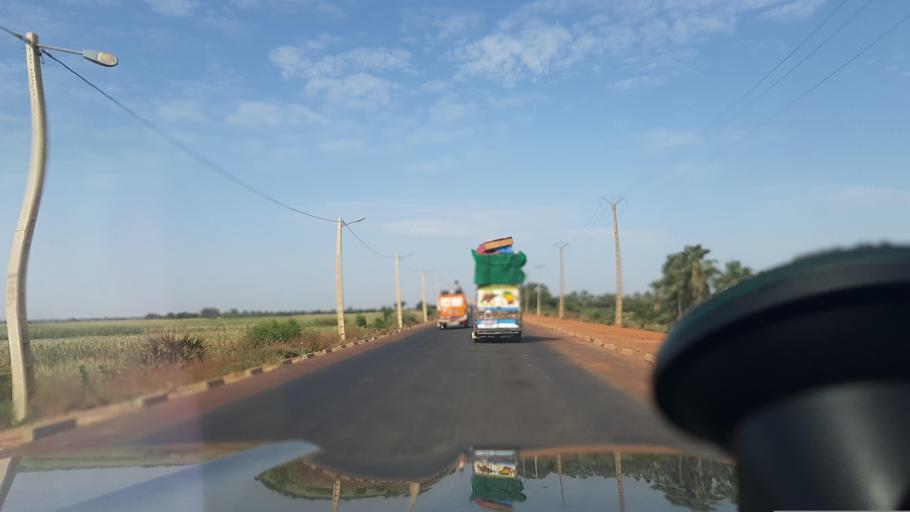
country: ML
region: Segou
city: Markala
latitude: 13.6829
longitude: -6.0901
